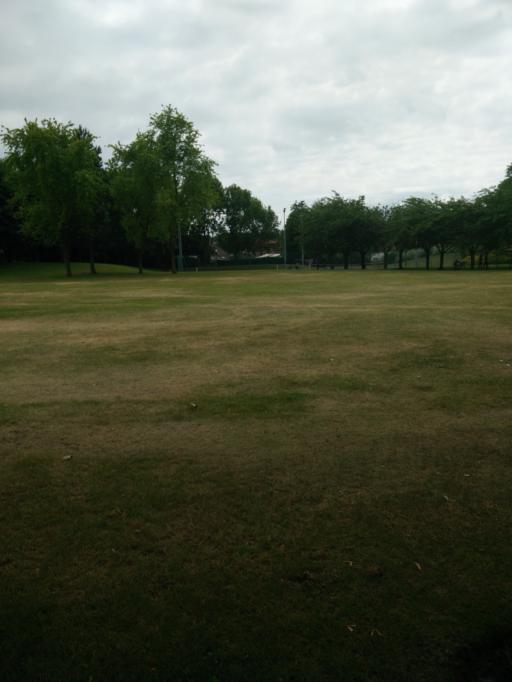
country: FR
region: Nord-Pas-de-Calais
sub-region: Departement du Pas-de-Calais
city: Grenay
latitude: 50.4485
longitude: 2.7393
